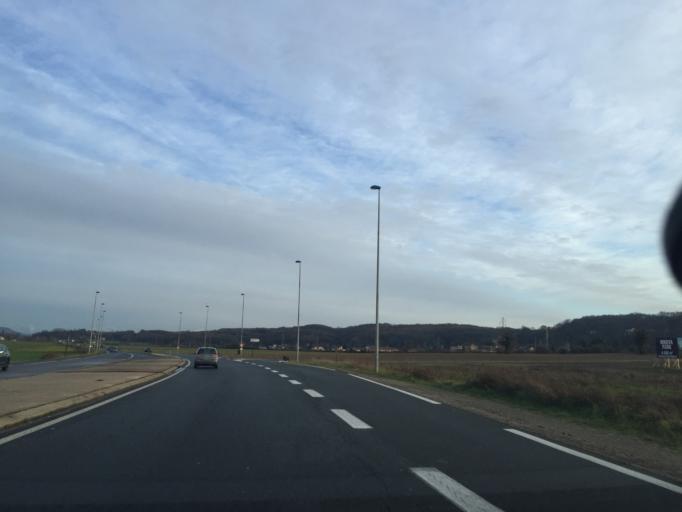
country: FR
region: Rhone-Alpes
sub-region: Departement de l'Isere
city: Vaulx-Milieu
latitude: 45.6188
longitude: 5.1831
